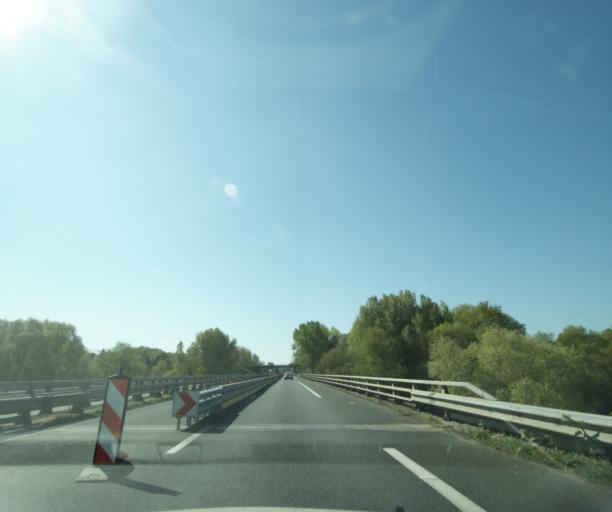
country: FR
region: Centre
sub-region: Departement du Cher
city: Vierzon
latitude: 47.2185
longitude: 2.0403
